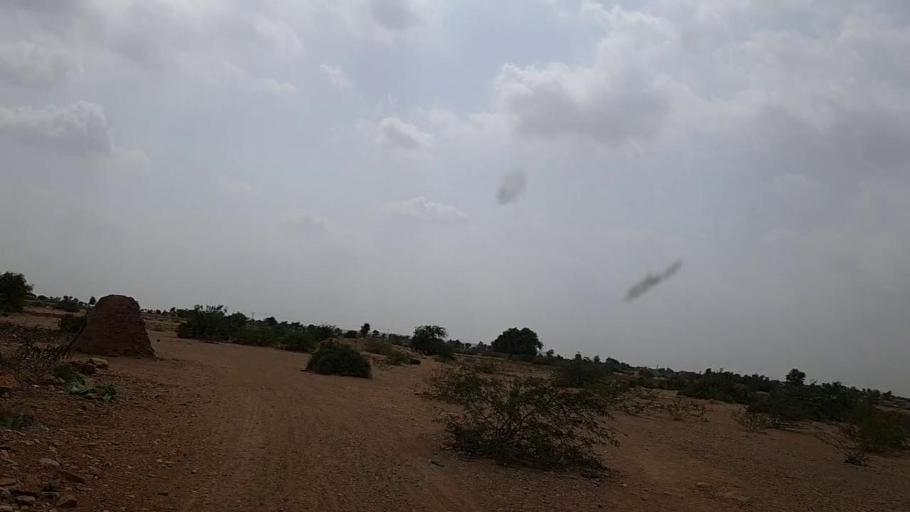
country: PK
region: Sindh
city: Kotri
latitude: 25.2896
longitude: 68.2136
